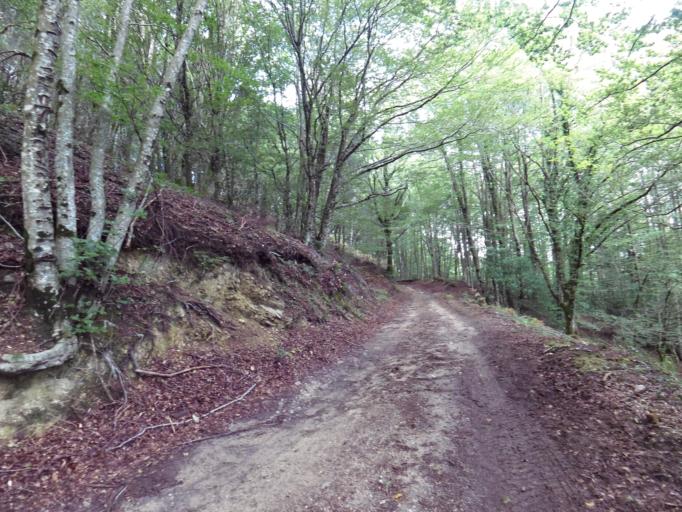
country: IT
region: Calabria
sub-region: Provincia di Vibo-Valentia
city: Nardodipace
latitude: 38.5220
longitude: 16.3839
